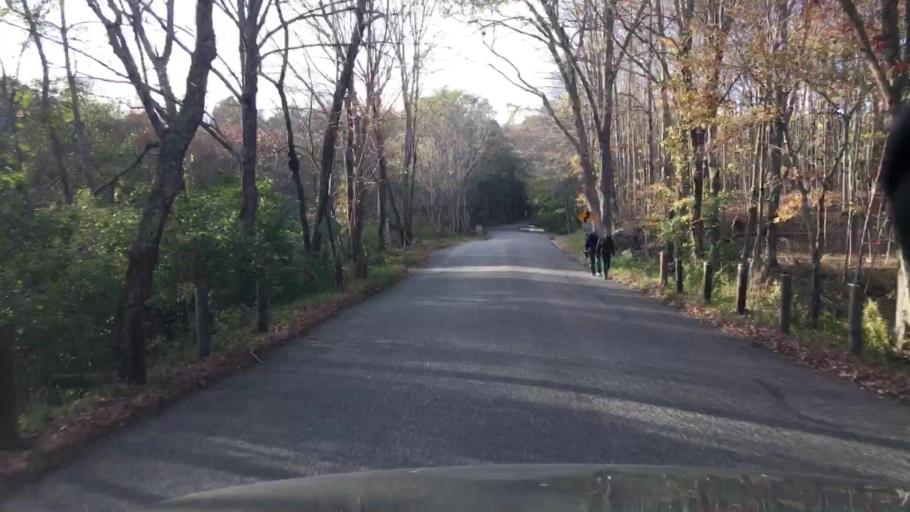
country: US
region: Connecticut
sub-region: Tolland County
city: Storrs
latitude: 41.8896
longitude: -72.1697
